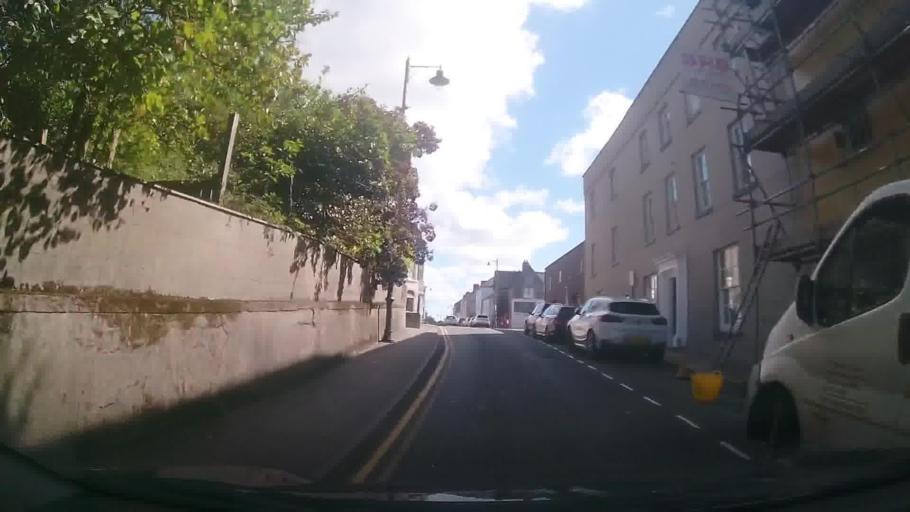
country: GB
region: Wales
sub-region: Pembrokeshire
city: Pembroke
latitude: 51.6749
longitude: -4.9136
